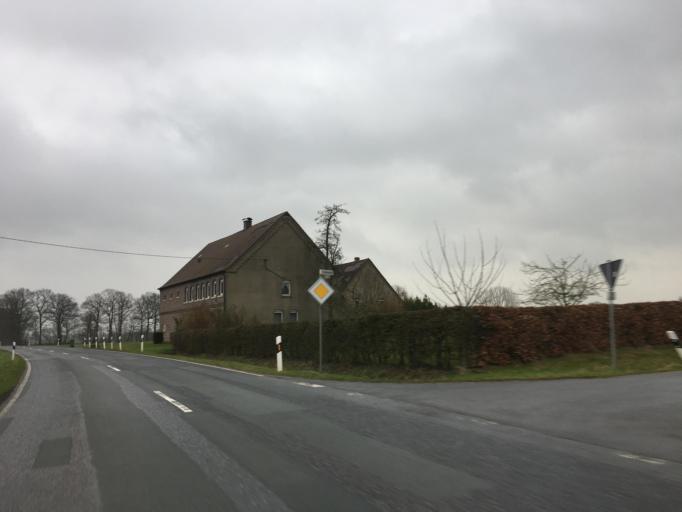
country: DE
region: North Rhine-Westphalia
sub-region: Regierungsbezirk Munster
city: Nottuln
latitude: 51.8620
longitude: 7.4044
